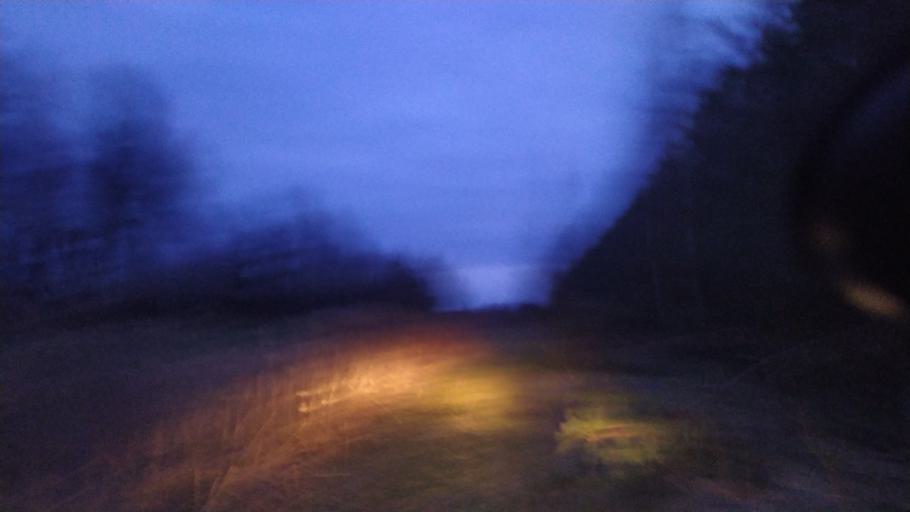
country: PL
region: Lublin Voivodeship
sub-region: Powiat lubelski
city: Jastkow
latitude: 51.3830
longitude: 22.4379
